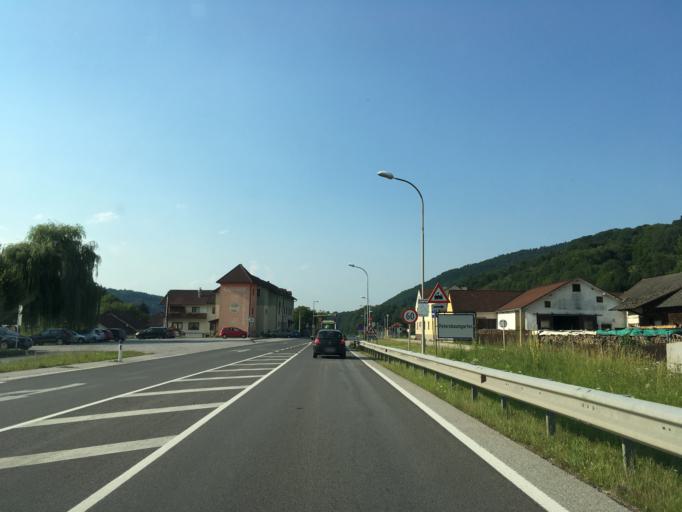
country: AT
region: Lower Austria
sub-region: Politischer Bezirk Neunkirchen
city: Grimmenstein
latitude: 47.6329
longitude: 16.1324
